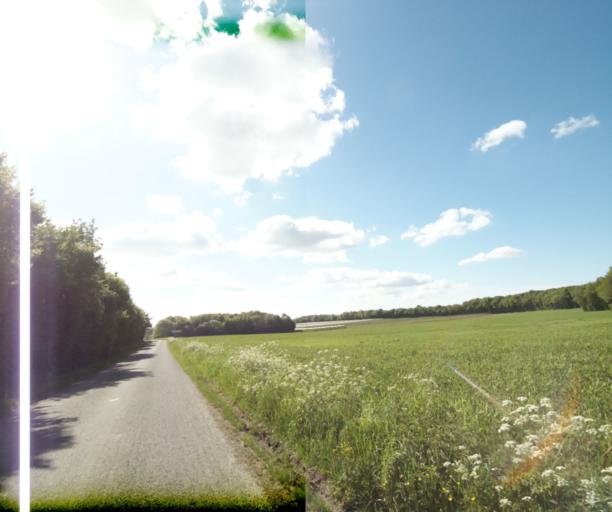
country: FR
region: Poitou-Charentes
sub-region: Departement de la Charente-Maritime
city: Chermignac
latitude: 45.7276
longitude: -0.6869
